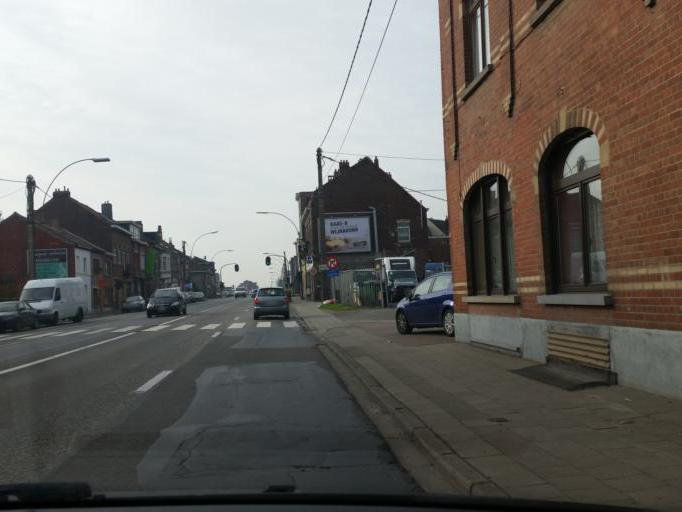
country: BE
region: Flanders
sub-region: Provincie Vlaams-Brabant
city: Drogenbos
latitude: 50.7934
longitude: 4.2831
